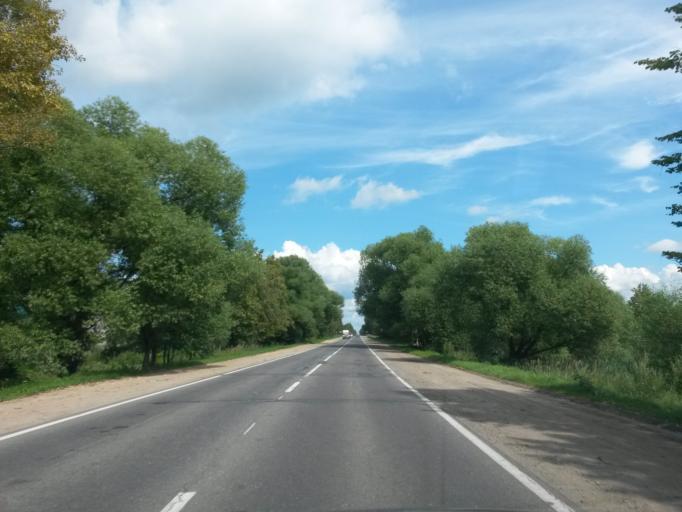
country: RU
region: Jaroslavl
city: Pereslavl'-Zalesskiy
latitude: 56.7674
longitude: 38.8735
